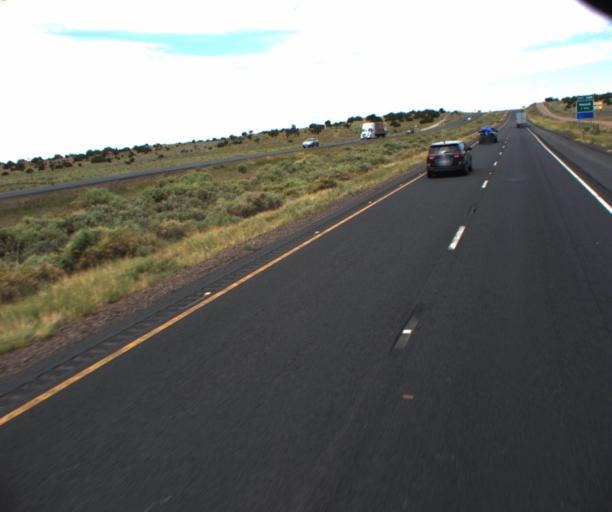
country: US
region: Arizona
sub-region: Apache County
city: Houck
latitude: 35.2811
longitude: -109.1902
